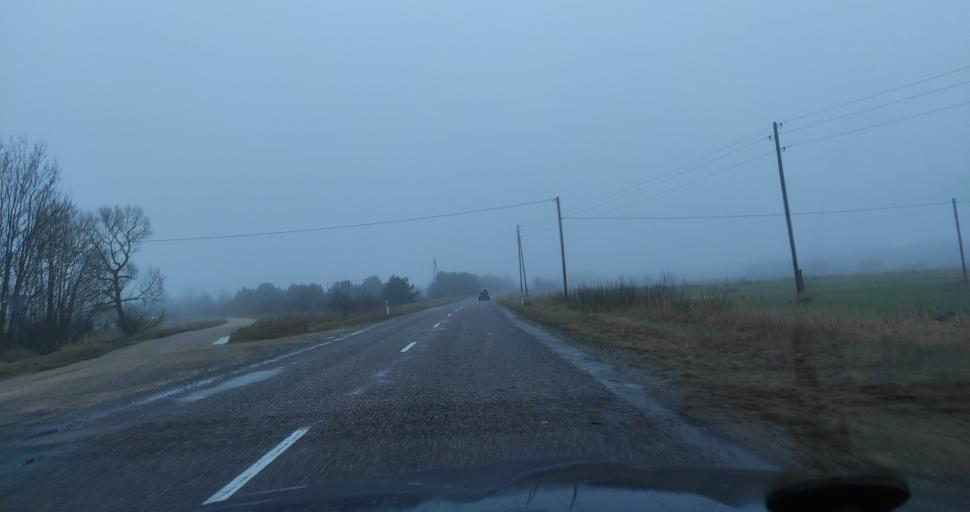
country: LV
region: Alsunga
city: Alsunga
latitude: 57.1201
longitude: 21.4248
